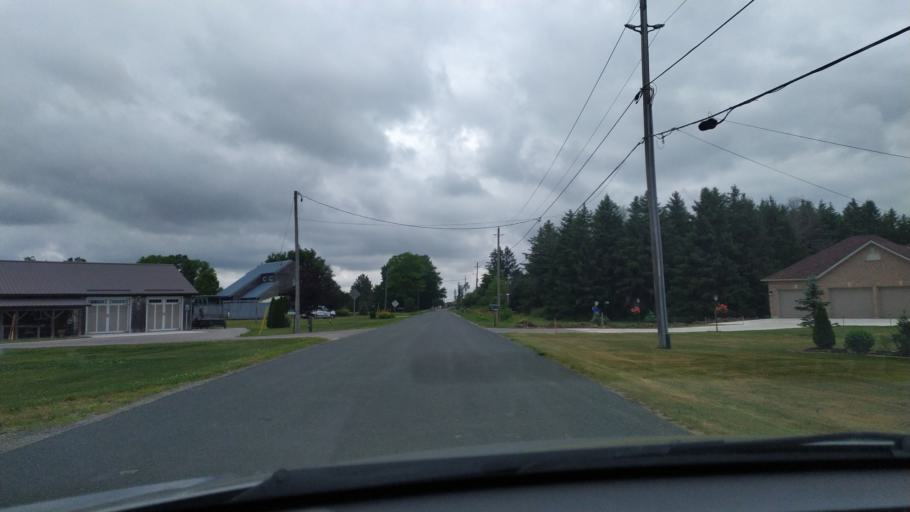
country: CA
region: Ontario
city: Stratford
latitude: 43.3675
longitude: -80.9318
